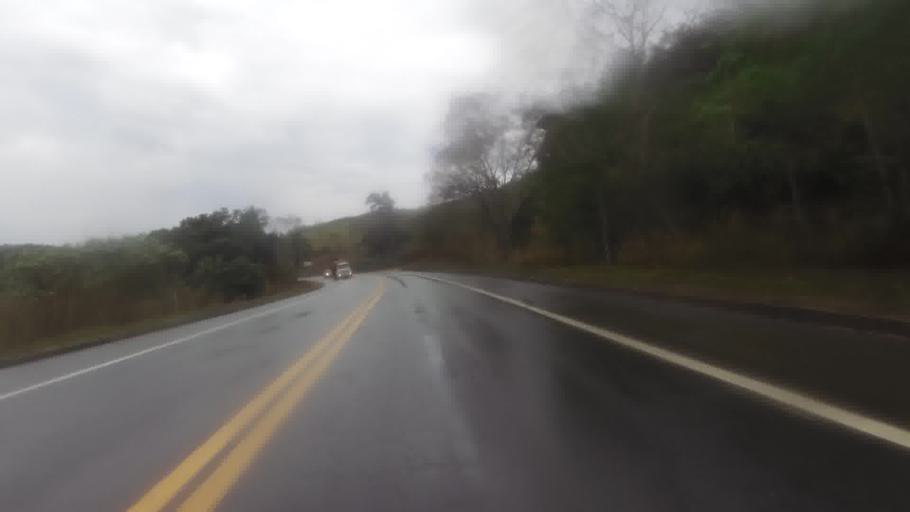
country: BR
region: Espirito Santo
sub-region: Cachoeiro De Itapemirim
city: Cachoeiro de Itapemirim
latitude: -21.0214
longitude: -41.1557
